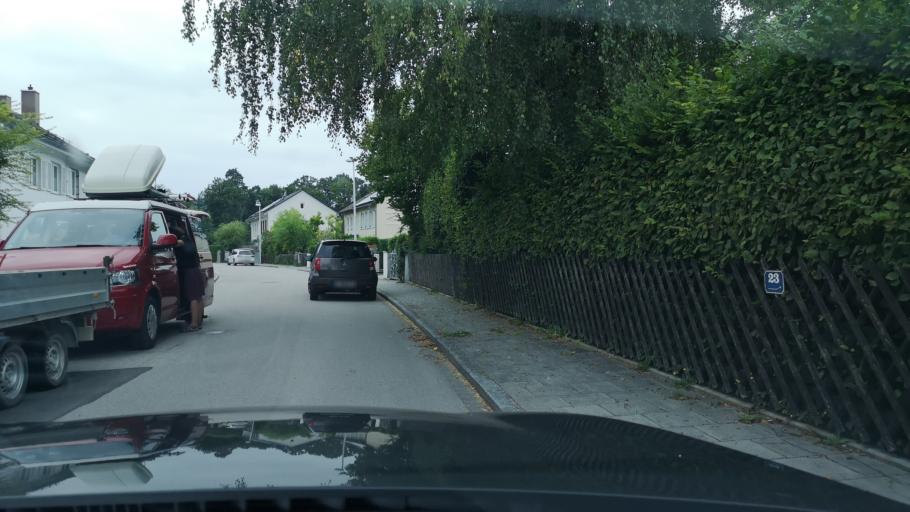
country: DE
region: Bavaria
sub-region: Upper Bavaria
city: Unterhaching
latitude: 48.0811
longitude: 11.6012
